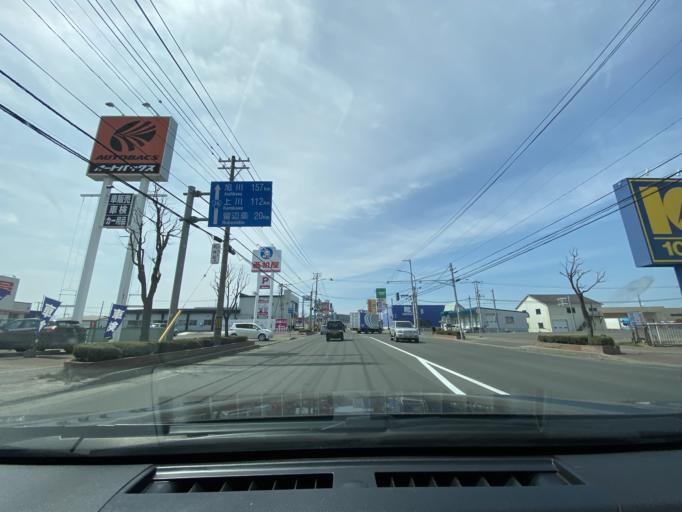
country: JP
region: Hokkaido
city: Kitami
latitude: 43.7978
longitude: 143.8549
